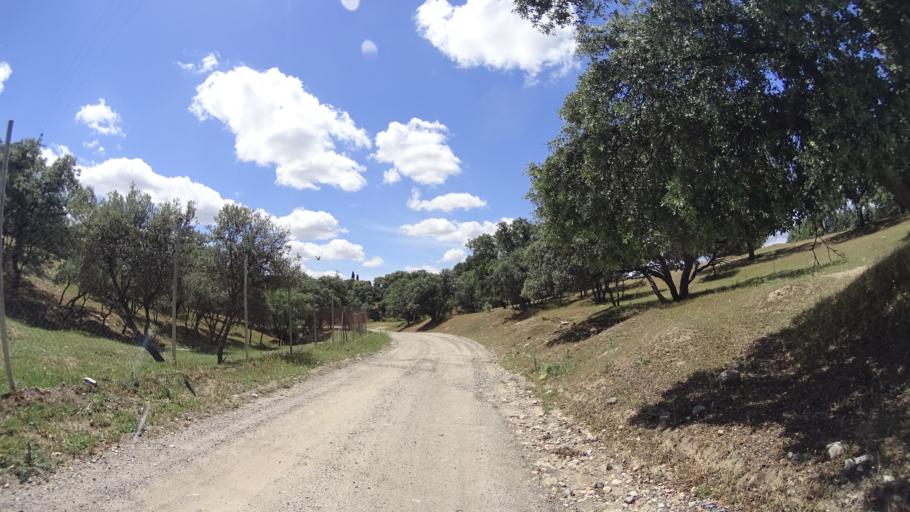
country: ES
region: Madrid
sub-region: Provincia de Madrid
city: Brunete
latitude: 40.4268
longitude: -3.9697
